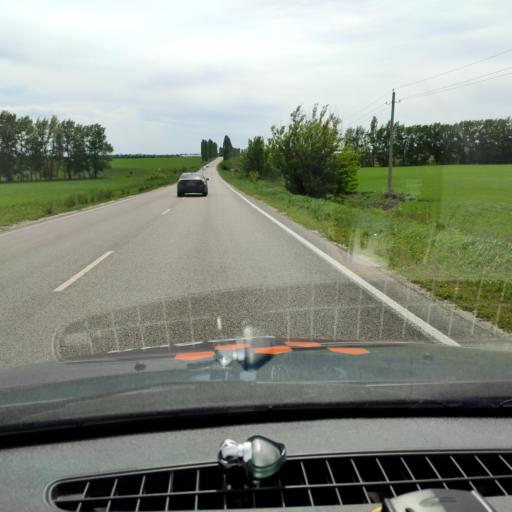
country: RU
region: Voronezj
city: Novaya Usman'
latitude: 51.5538
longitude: 39.3732
